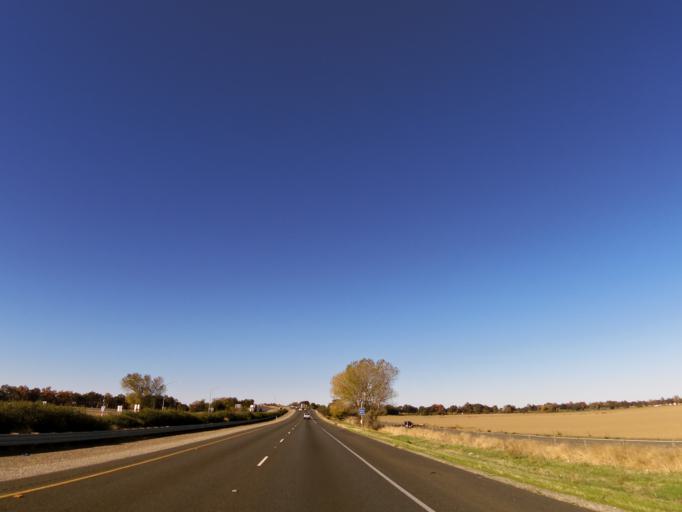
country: US
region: California
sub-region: Yolo County
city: West Sacramento
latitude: 38.6728
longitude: -121.6129
